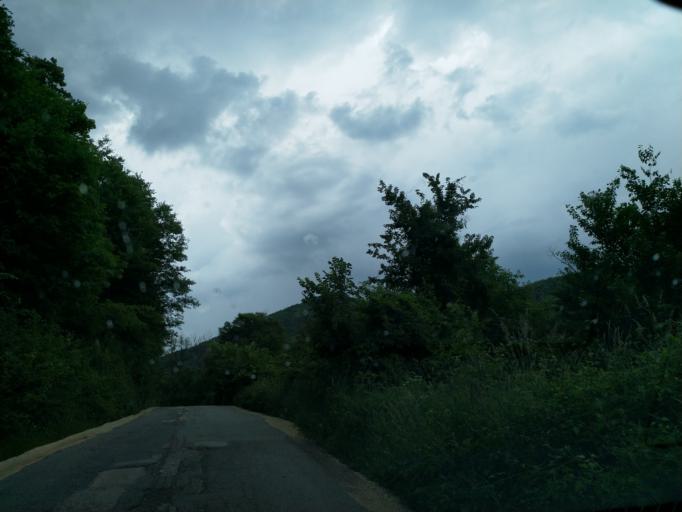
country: RS
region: Central Serbia
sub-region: Borski Okrug
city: Bor
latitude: 44.0231
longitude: 21.9782
